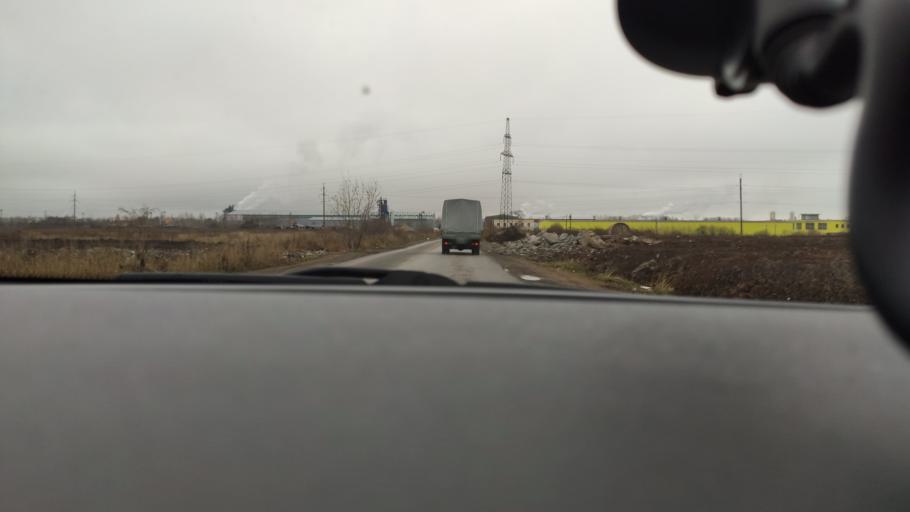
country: RU
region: Perm
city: Froly
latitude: 57.9121
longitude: 56.1873
